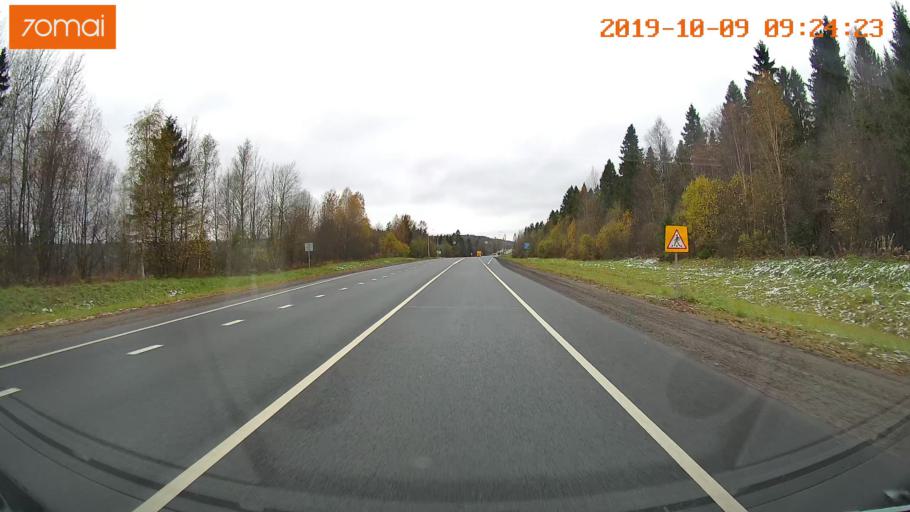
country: RU
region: Vologda
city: Vologda
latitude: 59.0783
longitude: 40.0170
